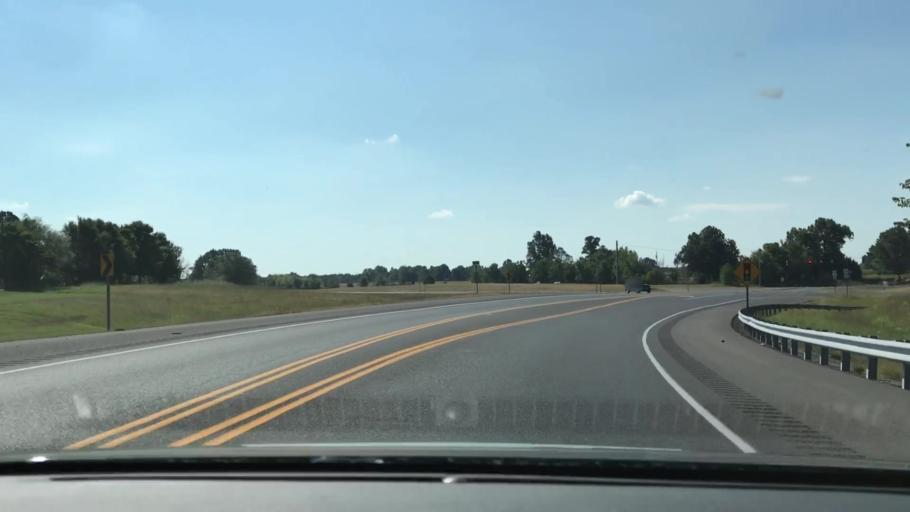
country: US
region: Kentucky
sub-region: Marshall County
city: Benton
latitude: 36.8162
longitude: -88.3499
